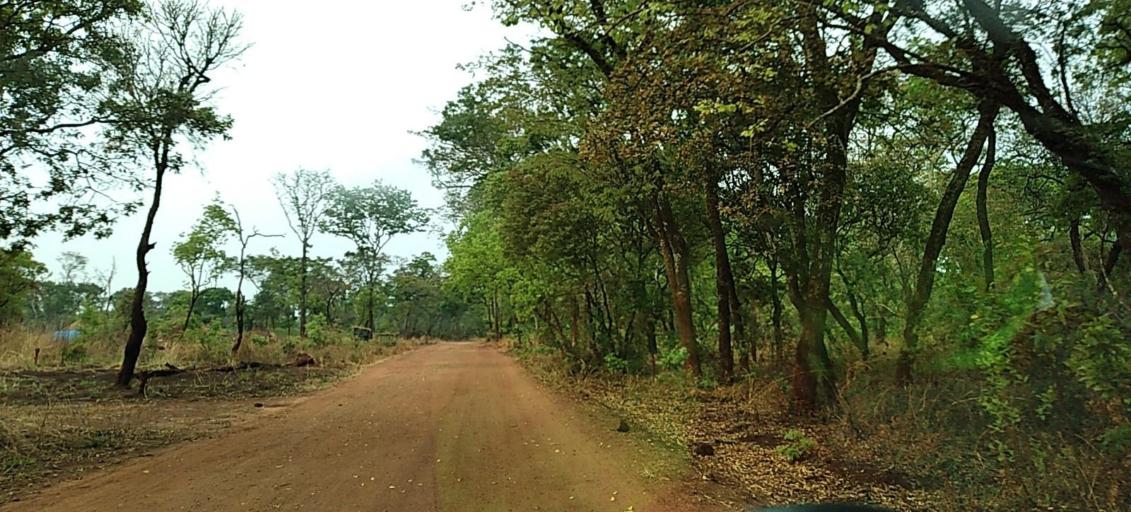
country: ZM
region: North-Western
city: Solwezi
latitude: -12.3071
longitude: 26.5228
